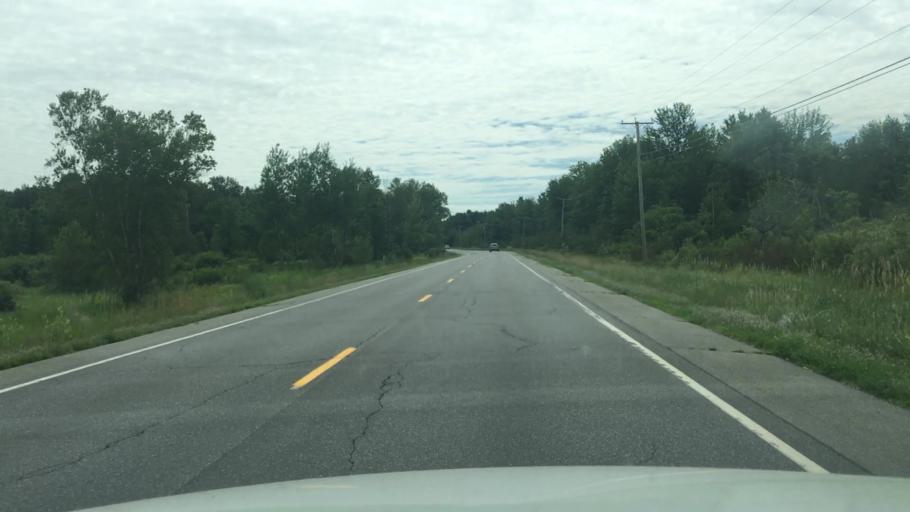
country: US
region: Maine
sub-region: Waldo County
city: Burnham
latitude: 44.6173
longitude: -69.3850
